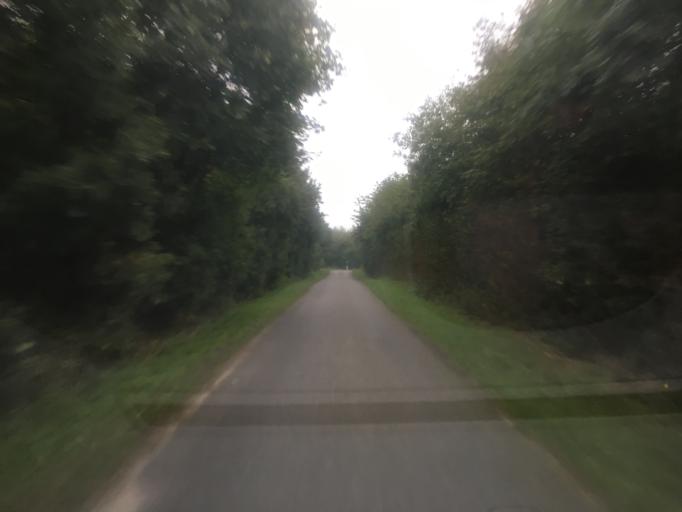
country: DK
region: South Denmark
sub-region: Tonder Kommune
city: Logumkloster
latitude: 55.0394
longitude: 8.9296
